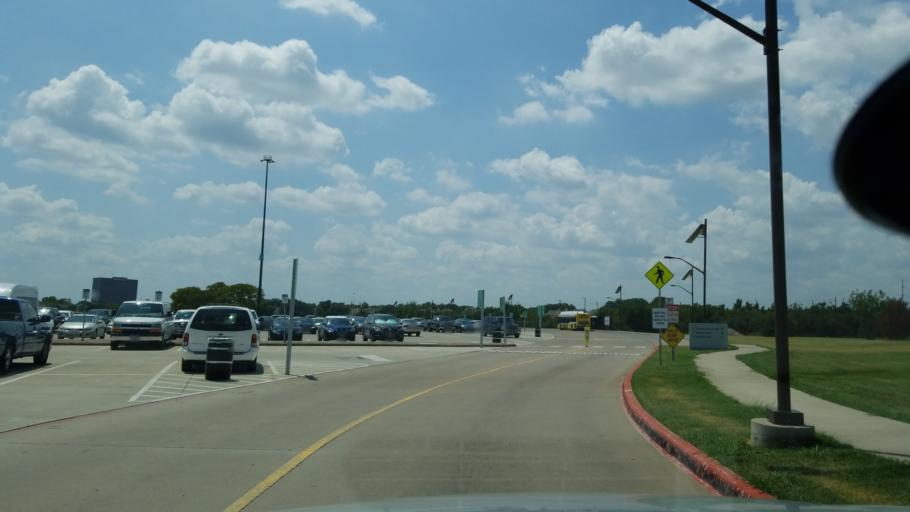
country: US
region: Texas
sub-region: Dallas County
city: Richardson
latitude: 32.9243
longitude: -96.7327
